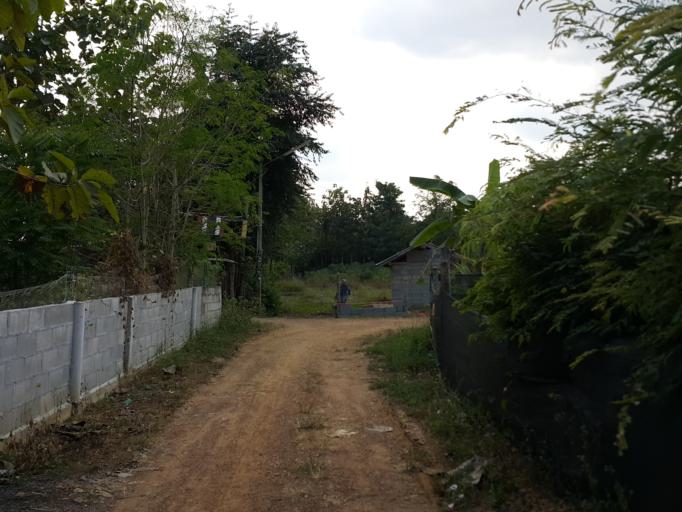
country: TH
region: Sukhothai
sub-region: Amphoe Si Satchanalai
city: Si Satchanalai
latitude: 17.4583
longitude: 99.6672
